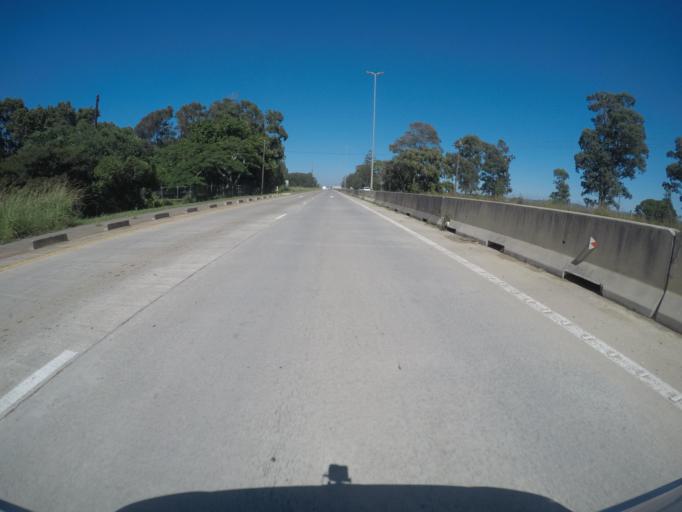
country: ZA
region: Eastern Cape
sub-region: Buffalo City Metropolitan Municipality
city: East London
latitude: -32.9379
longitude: 27.9814
